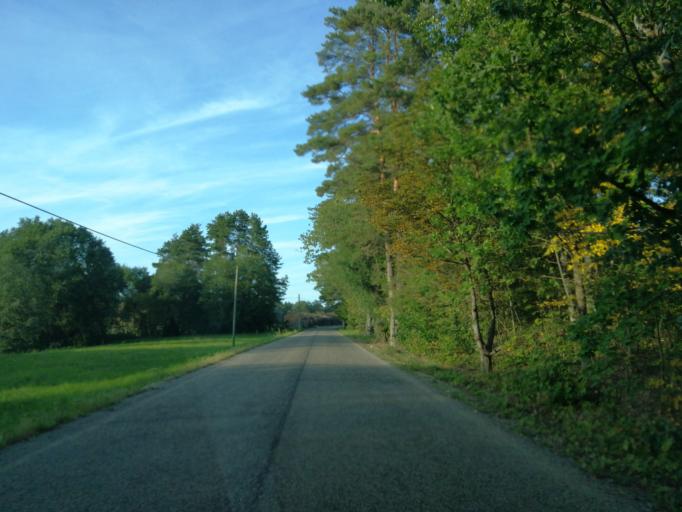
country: LV
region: Garkalne
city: Garkalne
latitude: 57.0772
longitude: 24.4592
